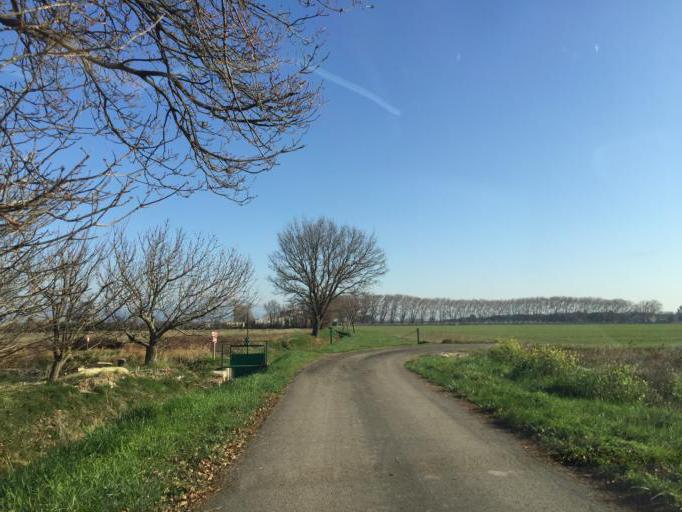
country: FR
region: Provence-Alpes-Cote d'Azur
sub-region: Departement du Vaucluse
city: Courthezon
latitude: 44.1208
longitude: 4.8576
